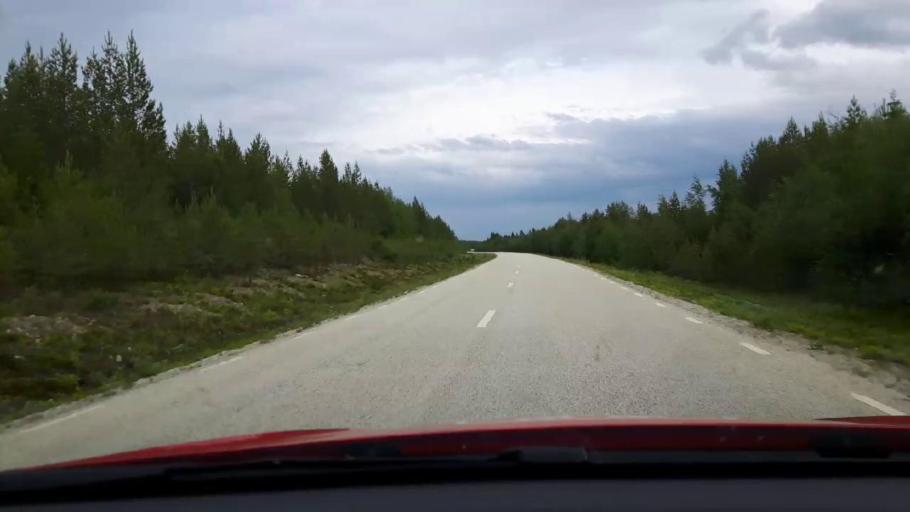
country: SE
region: Jaemtland
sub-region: Bergs Kommun
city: Hoverberg
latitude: 62.6987
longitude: 13.9604
